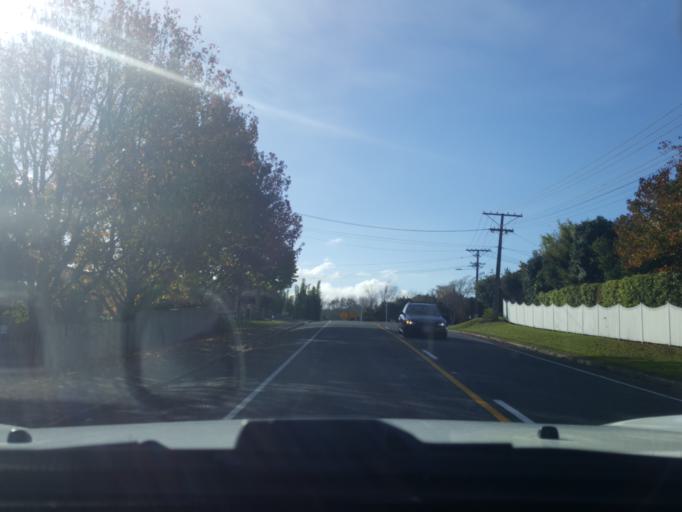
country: NZ
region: Auckland
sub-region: Auckland
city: Muriwai Beach
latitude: -36.7751
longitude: 174.5640
